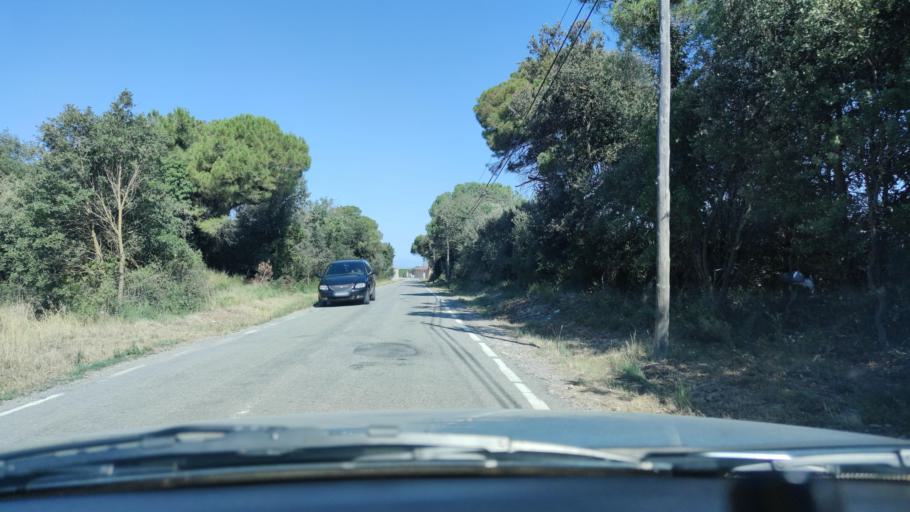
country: ES
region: Catalonia
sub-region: Provincia de Lleida
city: Sant Guim de Freixenet
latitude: 41.6449
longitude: 1.4088
